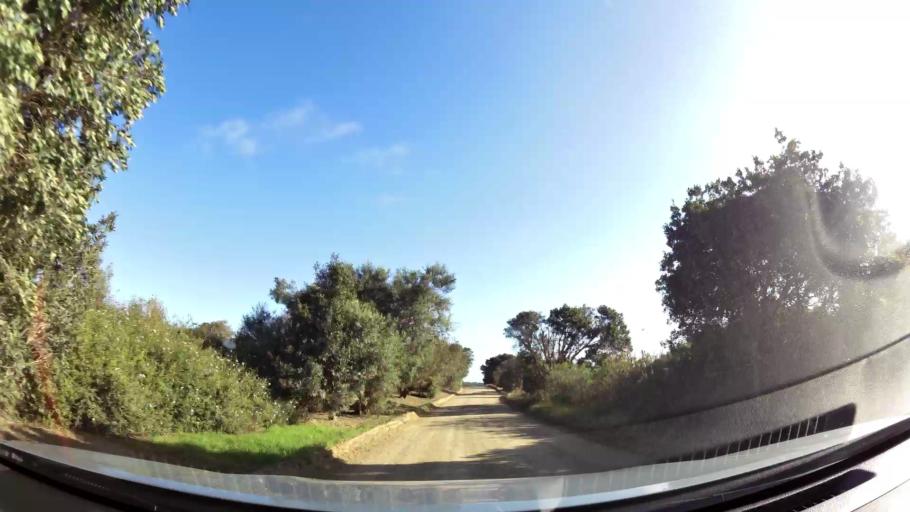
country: ZA
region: Western Cape
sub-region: Eden District Municipality
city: George
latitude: -33.9881
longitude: 22.5666
